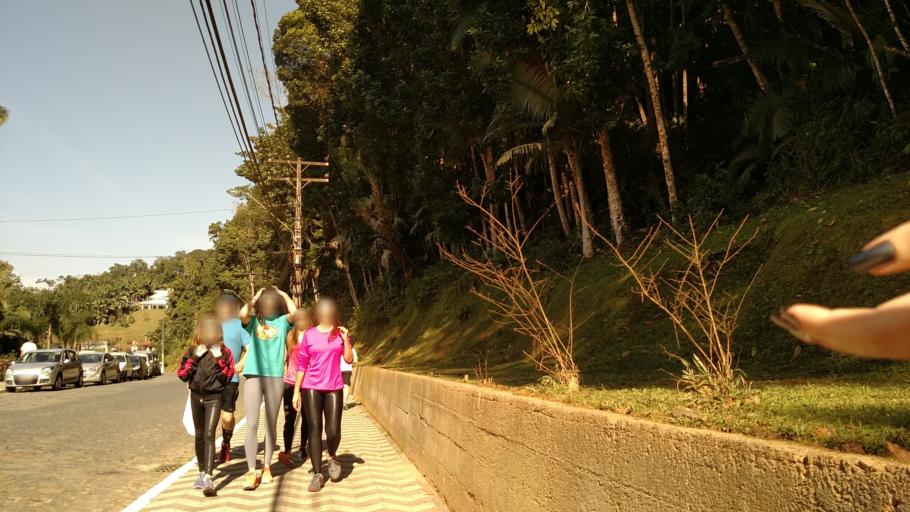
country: BR
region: Santa Catarina
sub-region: Pomerode
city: Pomerode
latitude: -26.7294
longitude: -49.0681
